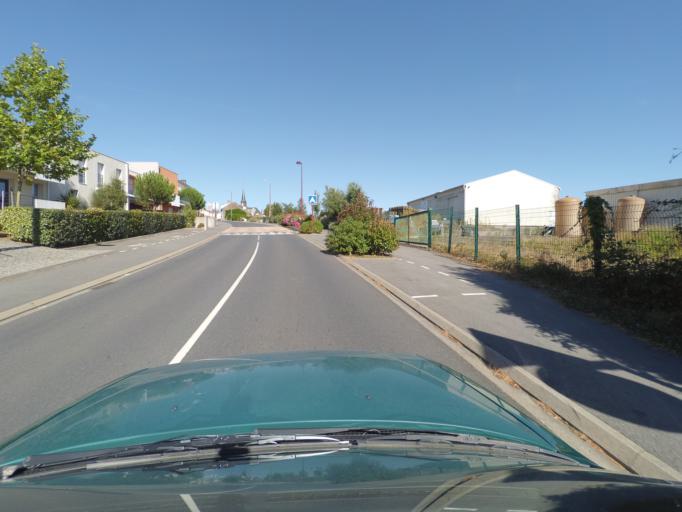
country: FR
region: Pays de la Loire
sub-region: Departement de la Loire-Atlantique
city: Maisdon-sur-Sevre
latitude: 47.0966
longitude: -1.3876
